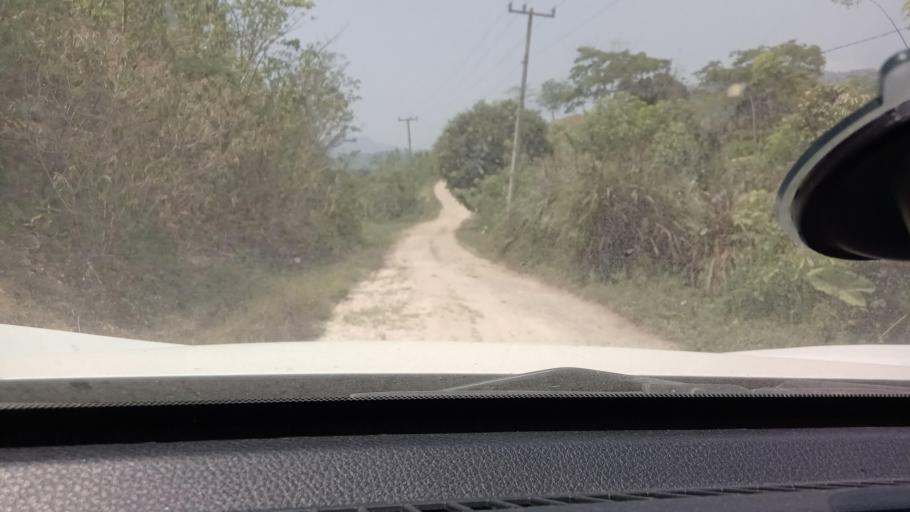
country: MX
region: Tabasco
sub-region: Huimanguillo
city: Francisco Rueda
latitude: 17.4781
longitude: -93.9463
